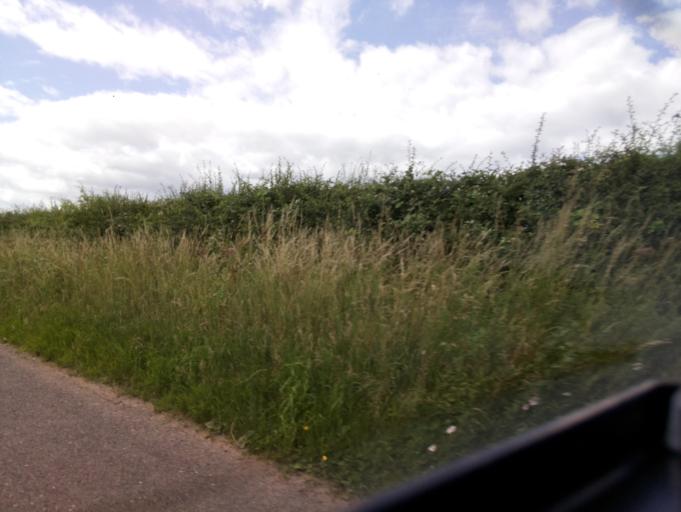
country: GB
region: England
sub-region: Nottinghamshire
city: Ruddington
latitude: 52.8579
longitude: -1.0996
